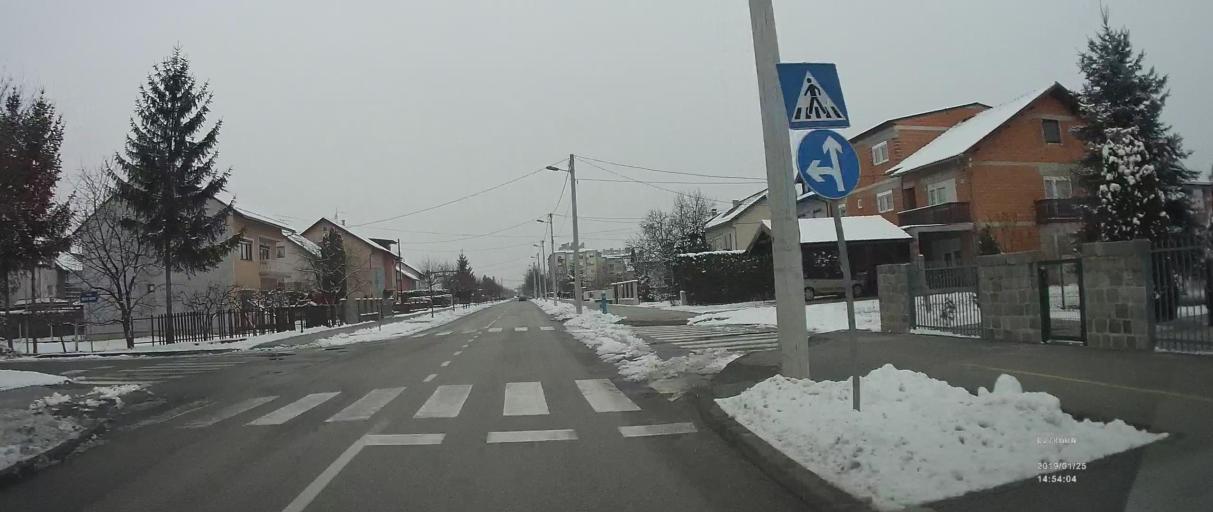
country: HR
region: Zagrebacka
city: Gradici
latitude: 45.7050
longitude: 16.0602
